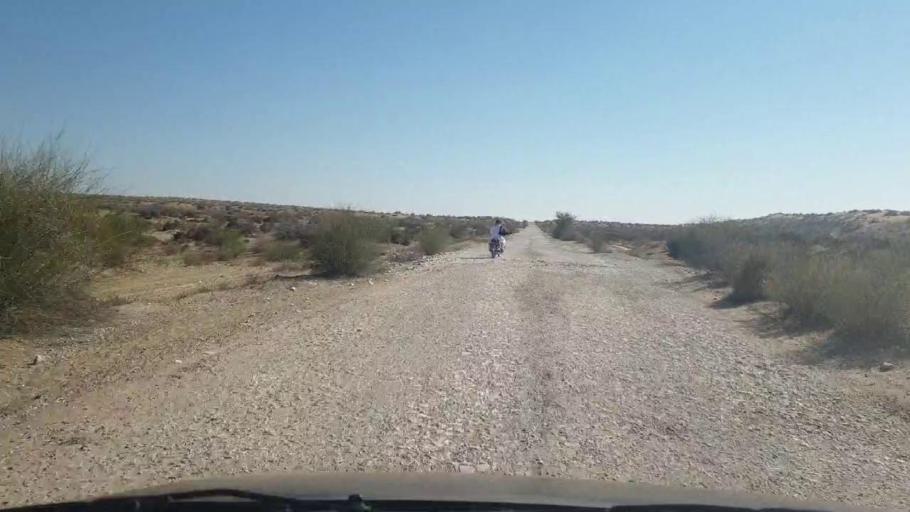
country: PK
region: Sindh
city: Bozdar
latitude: 27.0293
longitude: 68.7063
